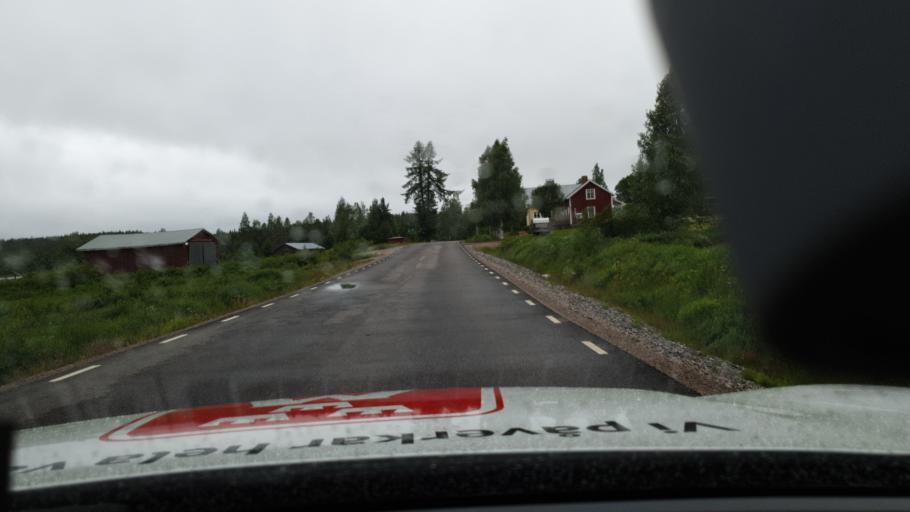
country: SE
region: Norrbotten
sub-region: Overtornea Kommun
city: OEvertornea
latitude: 66.4813
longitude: 23.4604
